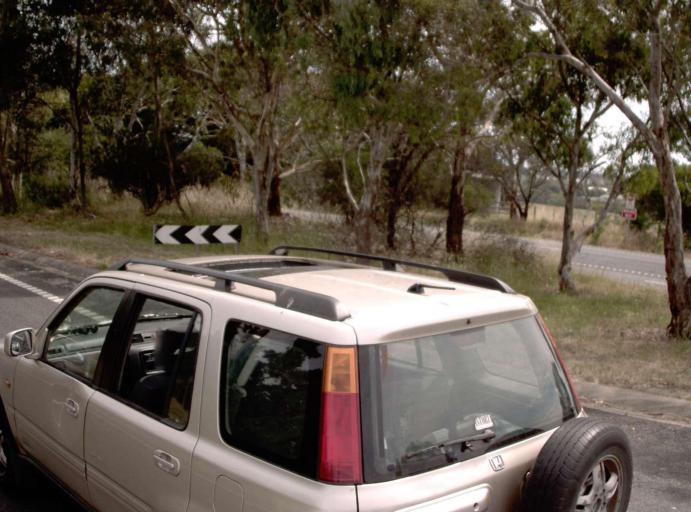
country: AU
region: Victoria
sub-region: Mornington Peninsula
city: Moorooduc
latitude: -38.2494
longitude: 145.0821
